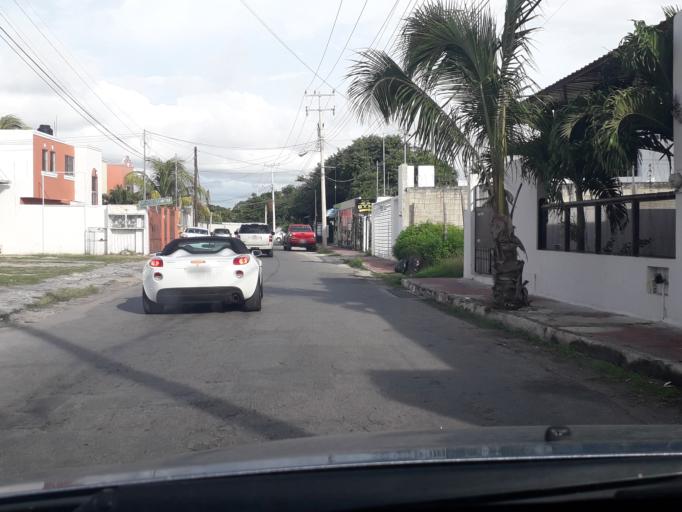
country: MX
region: Yucatan
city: Merida
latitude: 21.0039
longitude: -89.6406
